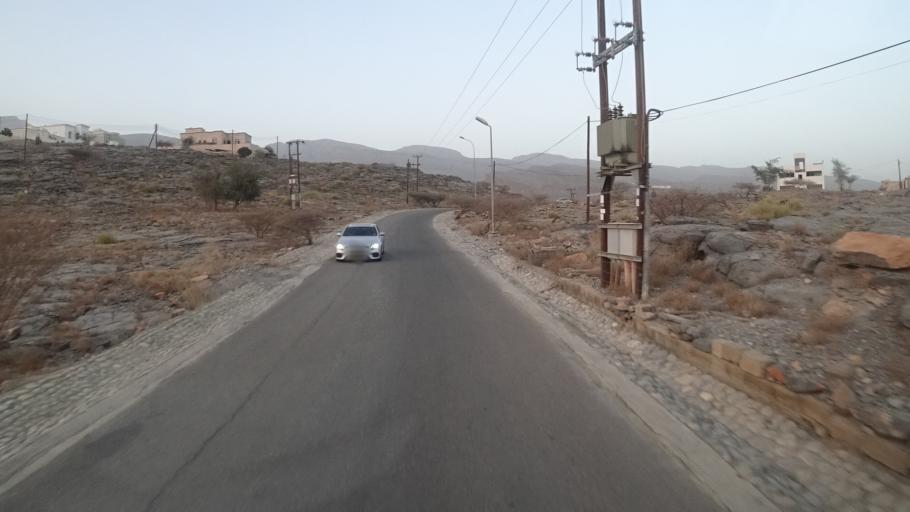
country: OM
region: Muhafazat ad Dakhiliyah
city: Bahla'
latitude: 23.1360
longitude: 57.3036
